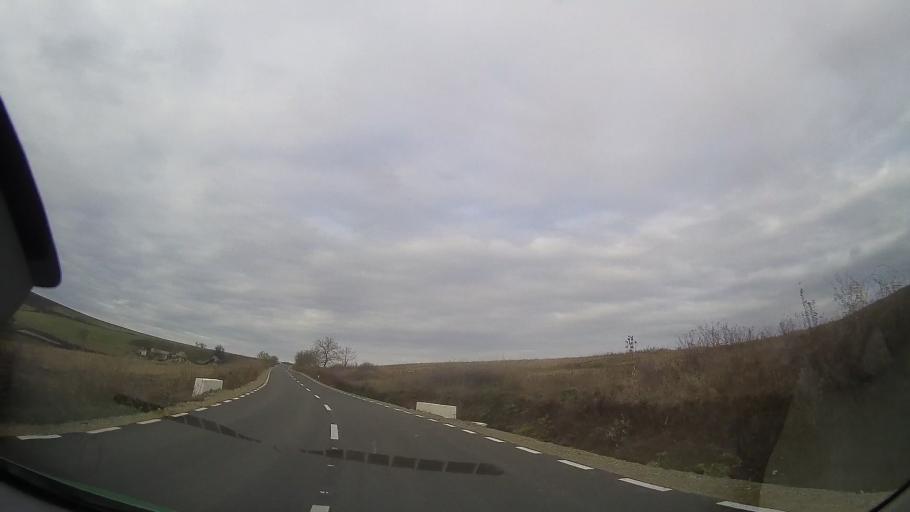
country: RO
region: Bistrita-Nasaud
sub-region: Comuna Teaca
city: Ocnita
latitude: 46.8257
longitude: 24.4788
